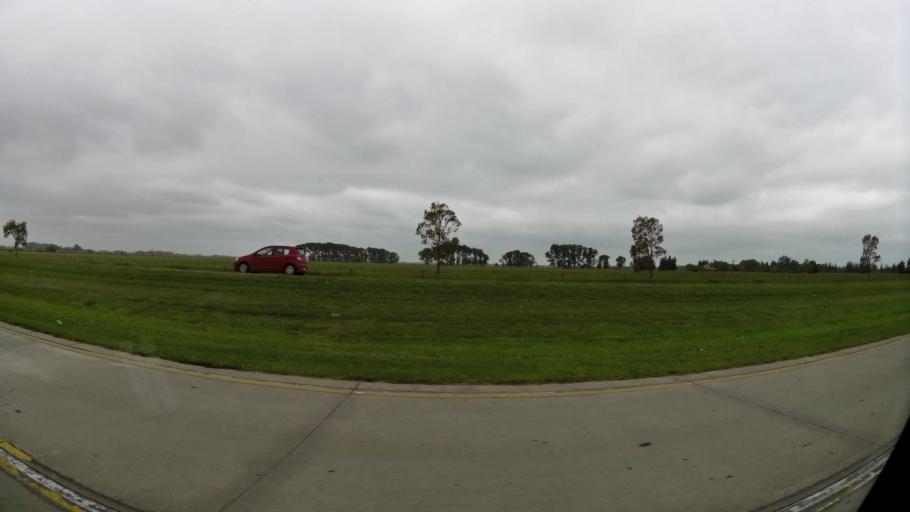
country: AR
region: Buenos Aires
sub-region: Partido de Brandsen
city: Brandsen
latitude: -35.0433
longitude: -58.1716
